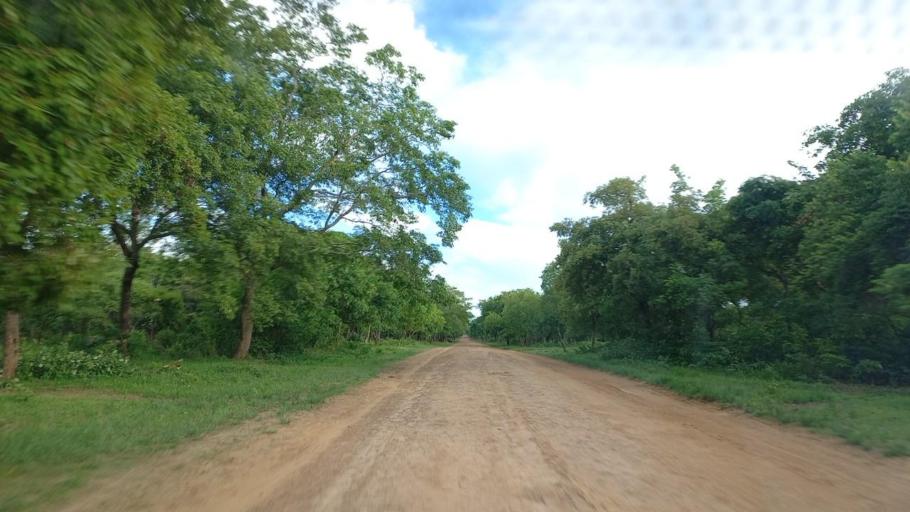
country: ZM
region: North-Western
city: Kabompo
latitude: -13.3712
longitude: 24.2972
